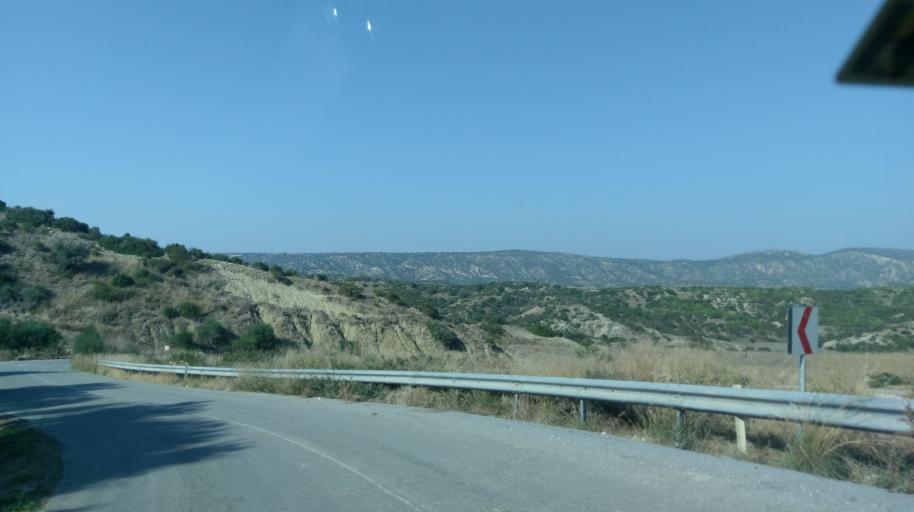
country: CY
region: Ammochostos
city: Leonarisso
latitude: 35.4957
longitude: 34.2259
